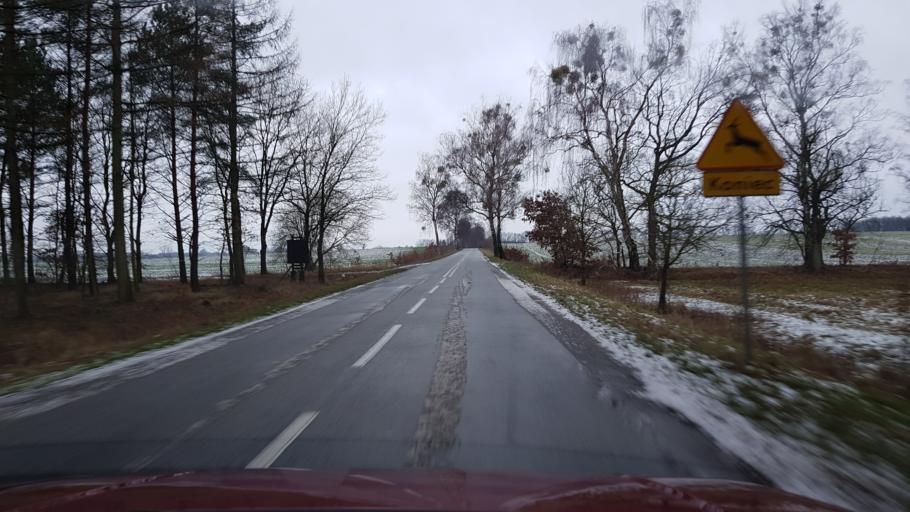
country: PL
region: West Pomeranian Voivodeship
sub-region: Powiat gryficki
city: Ploty
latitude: 53.7129
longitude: 15.2884
